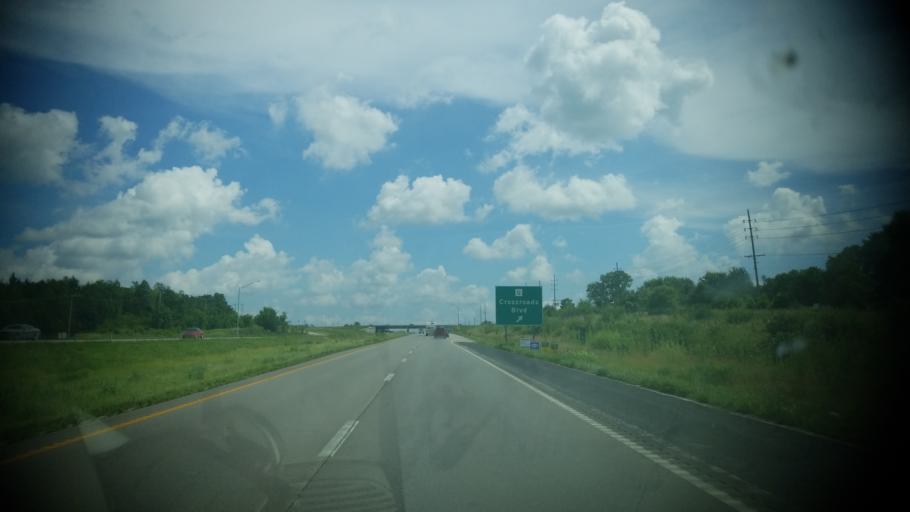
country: US
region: Missouri
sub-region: Lincoln County
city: Moscow Mills
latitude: 38.9141
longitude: -90.9243
